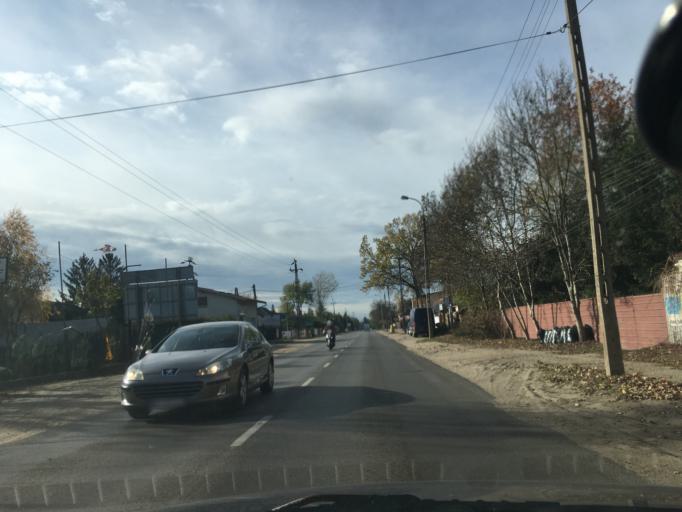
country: PL
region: Masovian Voivodeship
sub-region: Powiat piaseczynski
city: Piaseczno
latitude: 52.0515
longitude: 20.9978
